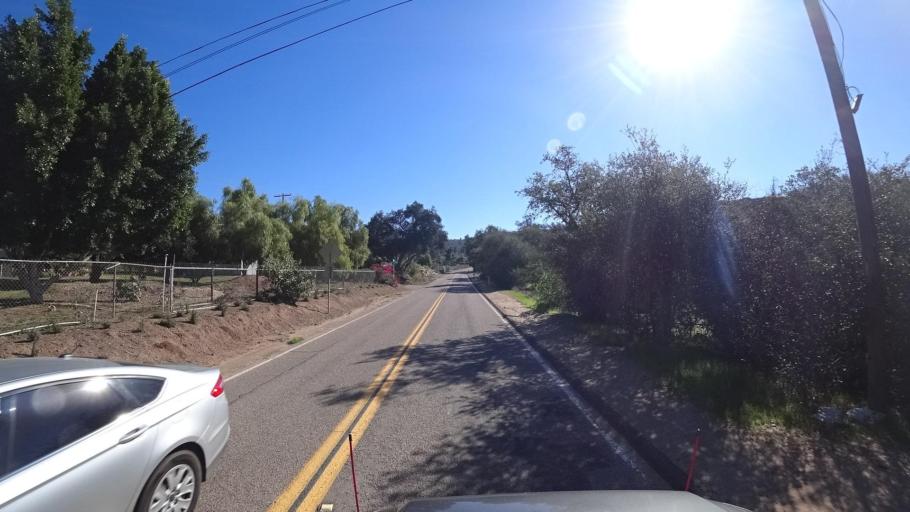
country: US
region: California
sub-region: San Diego County
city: Jamul
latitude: 32.7300
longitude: -116.8470
